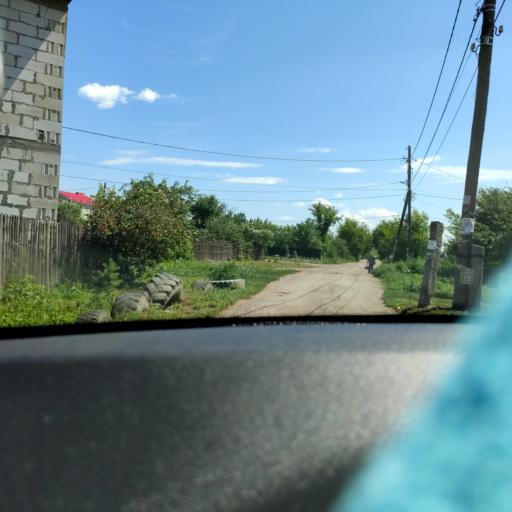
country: RU
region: Samara
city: Smyshlyayevka
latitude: 53.2434
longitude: 50.3526
